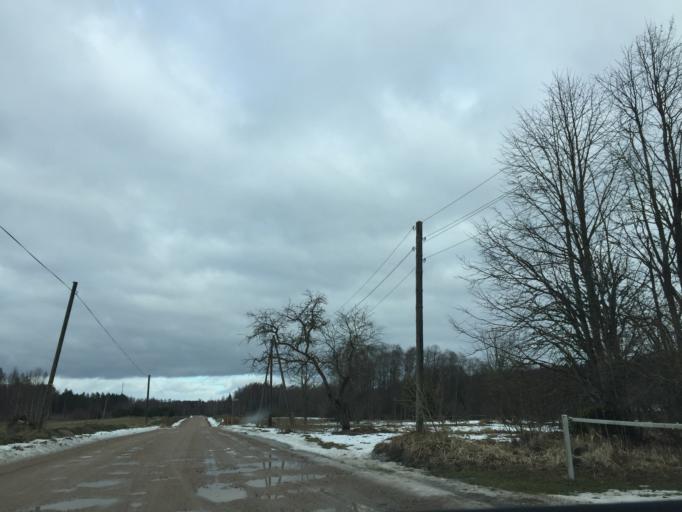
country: LV
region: Salacgrivas
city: Ainazi
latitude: 57.8520
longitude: 24.4894
